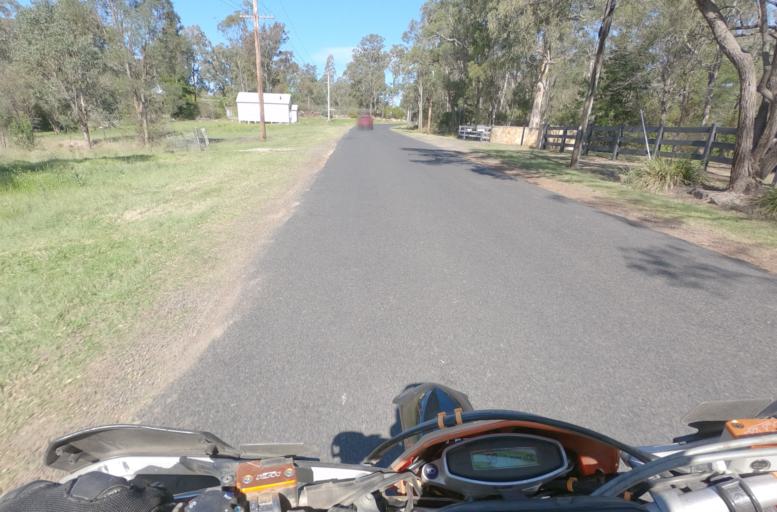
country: AU
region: New South Wales
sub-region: Hawkesbury
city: Scheyville
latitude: -33.5614
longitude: 150.9088
